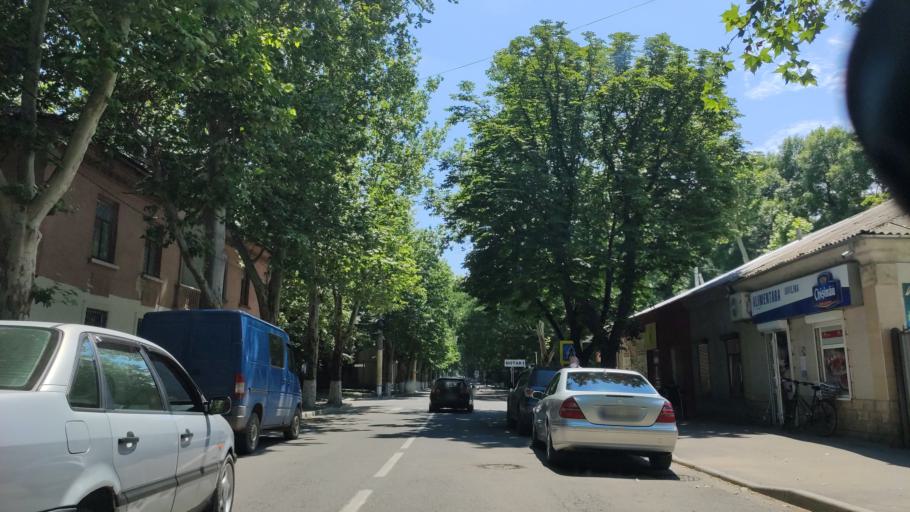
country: MD
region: Raionul Soroca
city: Soroca
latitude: 48.1543
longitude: 28.3001
